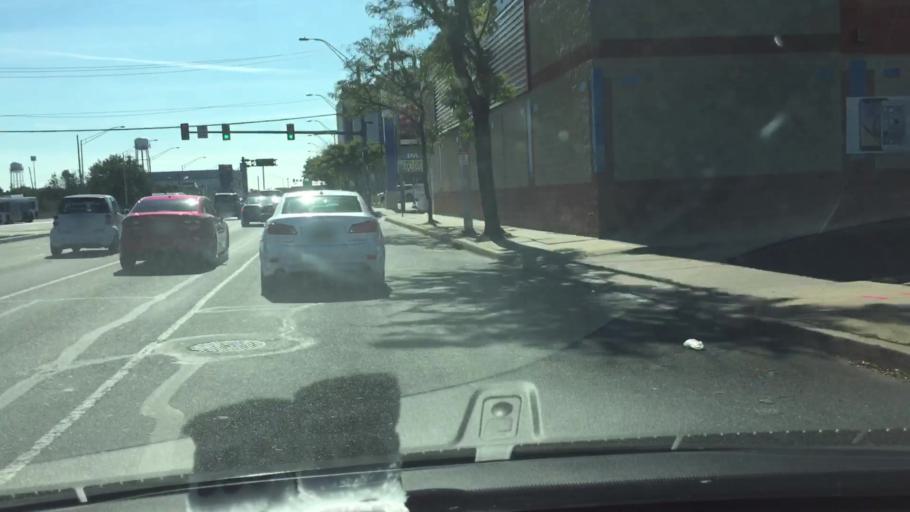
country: US
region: New Jersey
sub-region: Camden County
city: Camden
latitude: 39.9304
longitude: -75.1444
